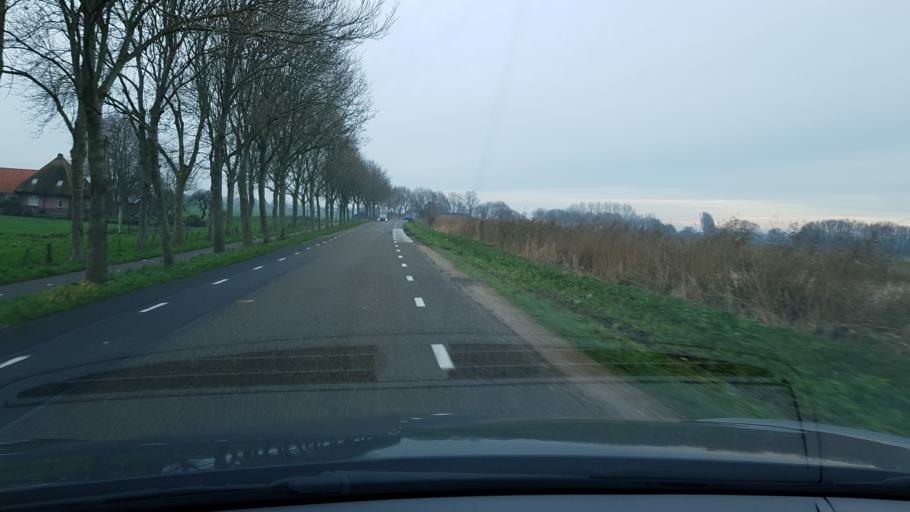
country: NL
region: North Holland
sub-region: Gemeente Uithoorn
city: Uithoorn
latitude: 52.2211
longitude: 4.8287
